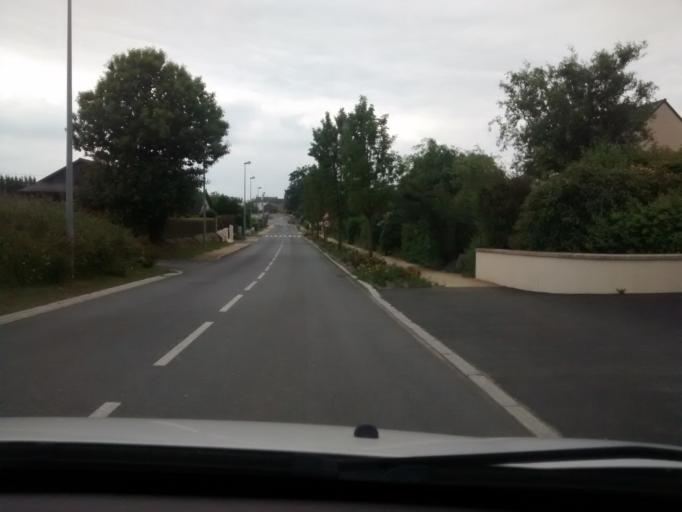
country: FR
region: Brittany
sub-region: Departement d'Ille-et-Vilaine
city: La Bouexiere
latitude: 48.1776
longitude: -1.4364
